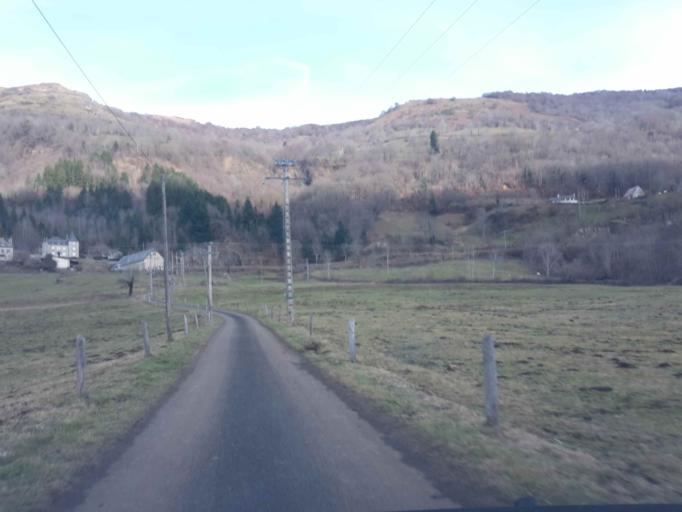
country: FR
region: Auvergne
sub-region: Departement du Cantal
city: Riom-es-Montagnes
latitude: 45.1787
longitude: 2.5848
